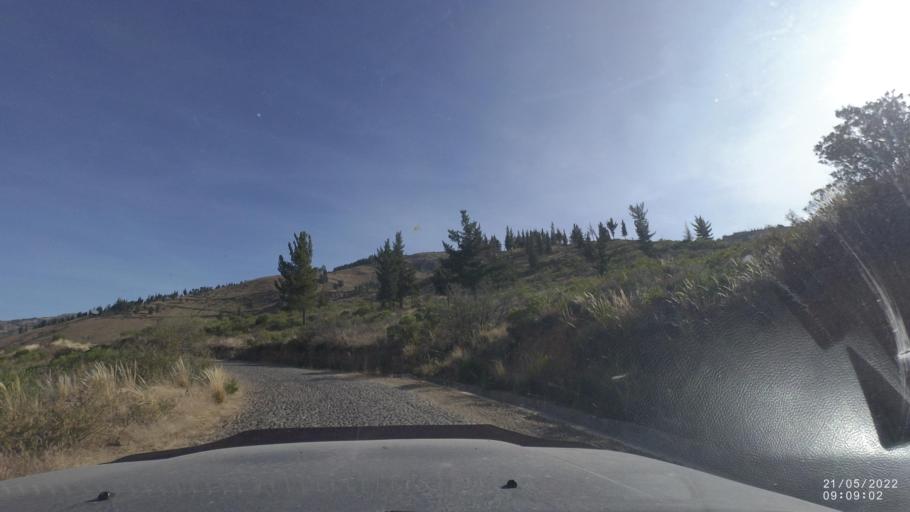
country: BO
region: Cochabamba
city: Cochabamba
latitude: -17.3754
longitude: -66.0232
